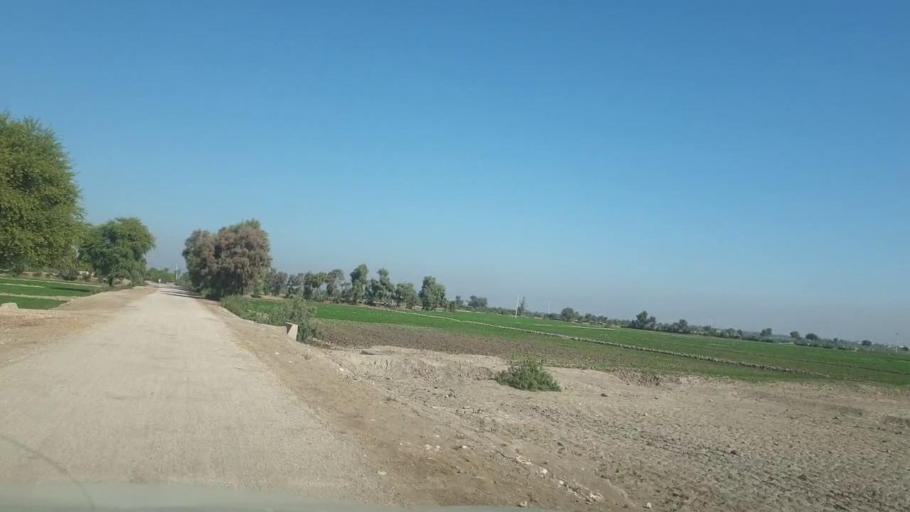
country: PK
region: Sindh
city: Bhan
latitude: 26.5266
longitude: 67.6436
